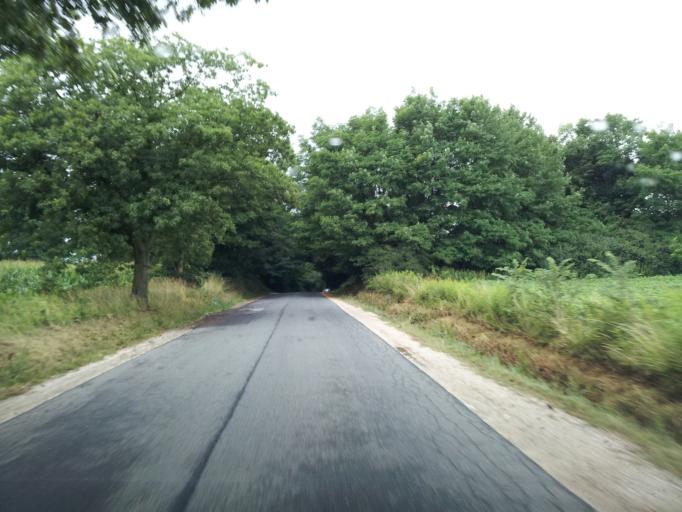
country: HU
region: Vas
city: Kormend
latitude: 46.9630
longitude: 16.6342
